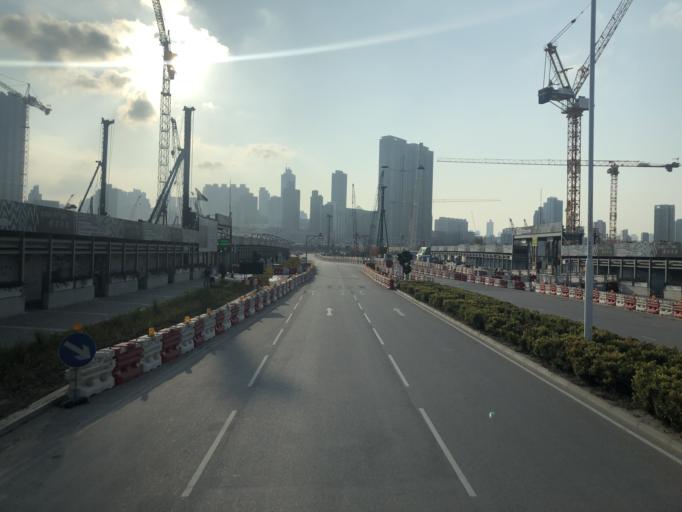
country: HK
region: Kowloon City
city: Kowloon
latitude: 22.3244
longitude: 114.1986
